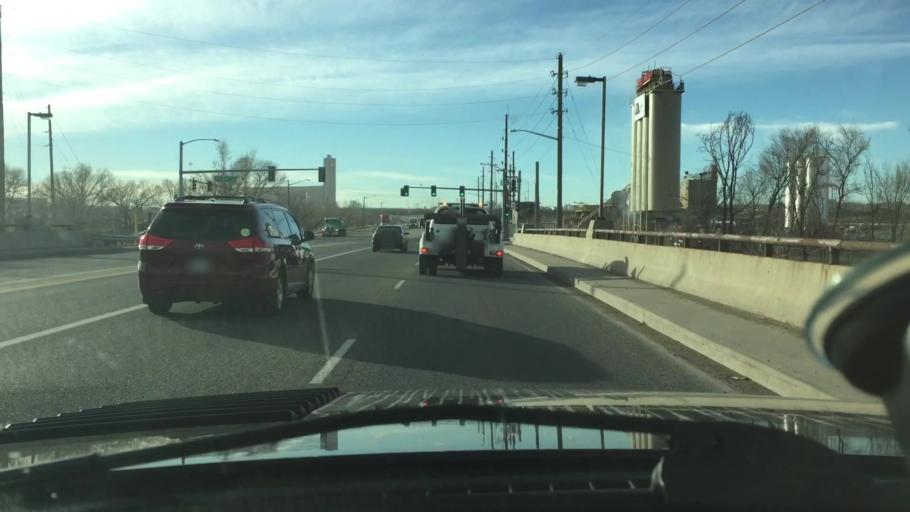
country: US
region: Colorado
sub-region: Adams County
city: Twin Lakes
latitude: 39.8134
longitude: -105.0060
